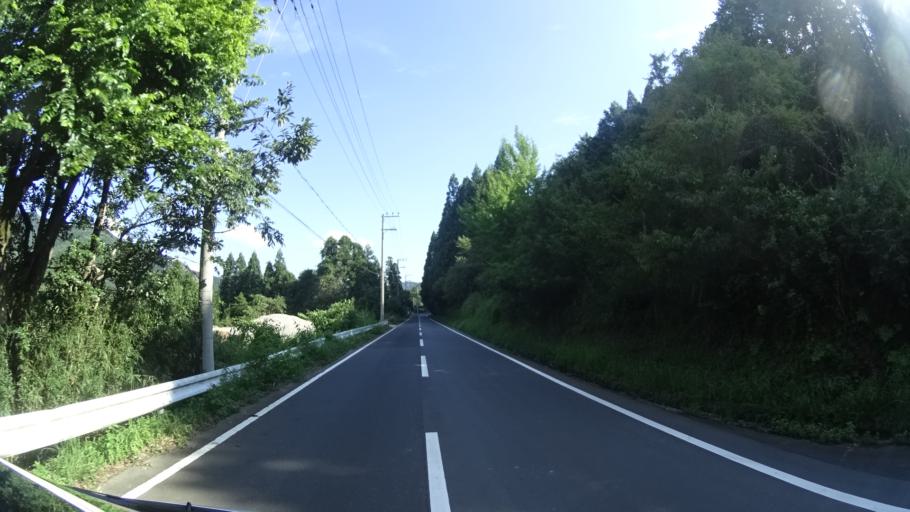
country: JP
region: Kyoto
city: Ayabe
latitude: 35.2934
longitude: 135.3276
